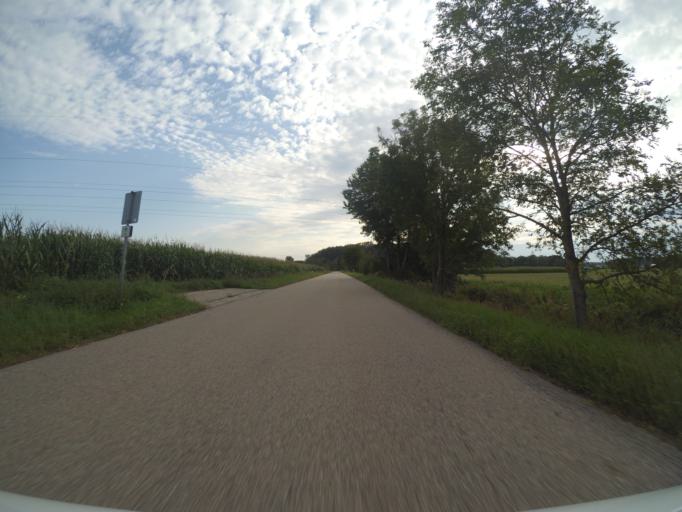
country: DE
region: Bavaria
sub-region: Upper Palatinate
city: Schwarzenfeld
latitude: 49.3981
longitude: 12.1498
